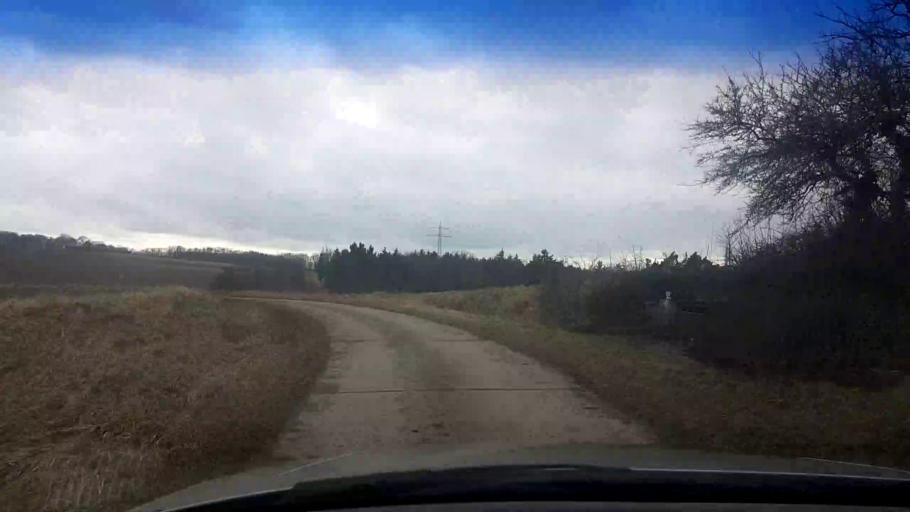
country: DE
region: Bavaria
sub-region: Regierungsbezirk Unterfranken
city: Stettfeld
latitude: 49.9428
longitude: 10.7137
